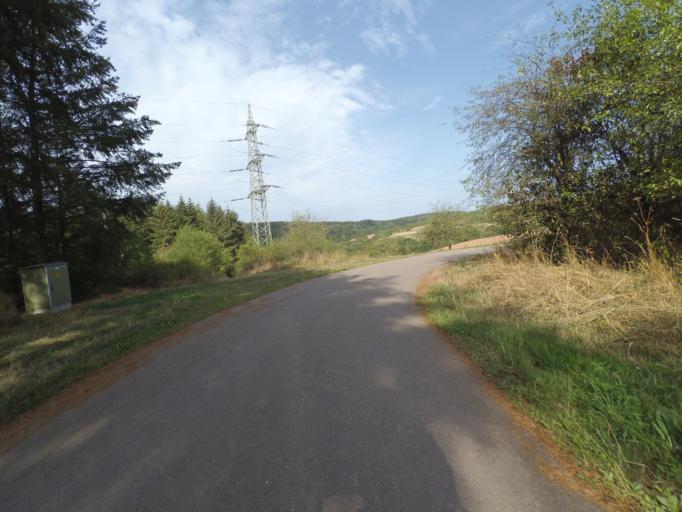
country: DE
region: Rheinland-Pfalz
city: Ayl
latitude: 49.6251
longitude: 6.5384
